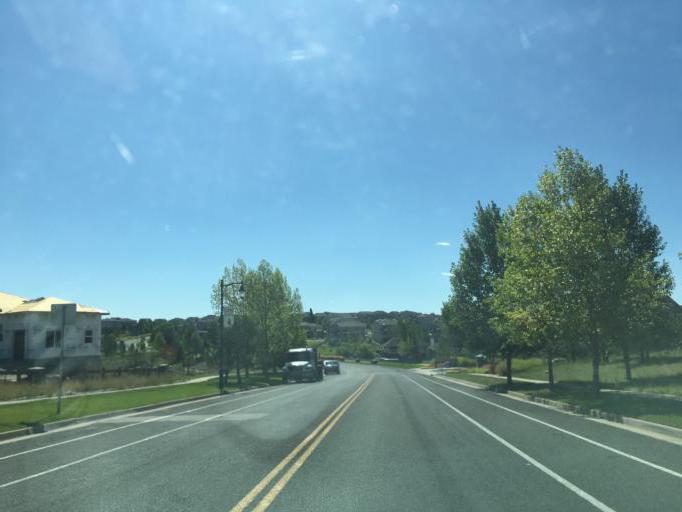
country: US
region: Colorado
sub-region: Douglas County
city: Parker
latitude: 39.5973
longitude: -104.6772
